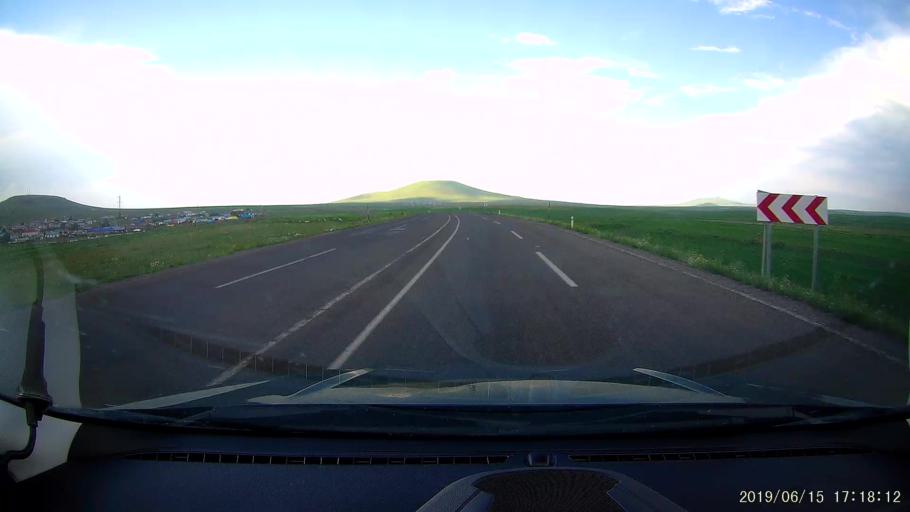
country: TR
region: Kars
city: Kars
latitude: 40.6130
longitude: 43.2531
